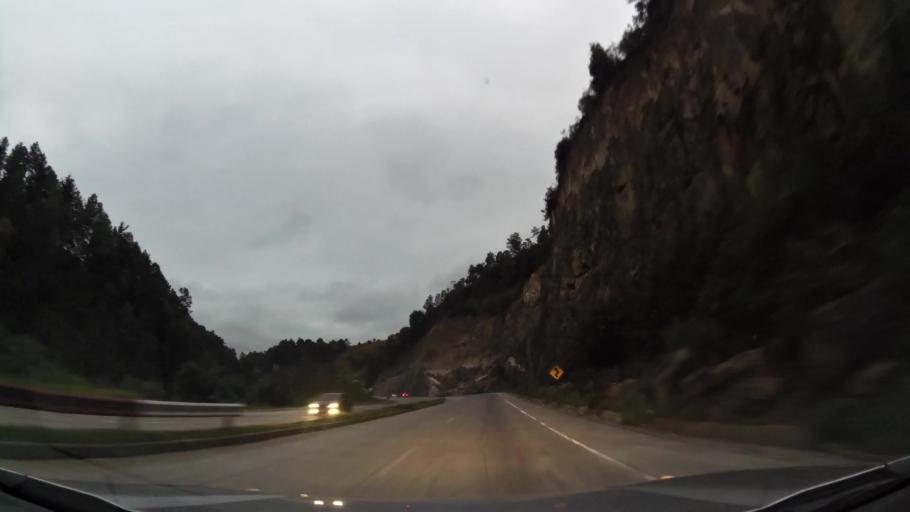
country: GT
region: Chimaltenango
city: Tecpan Guatemala
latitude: 14.8355
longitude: -91.0416
